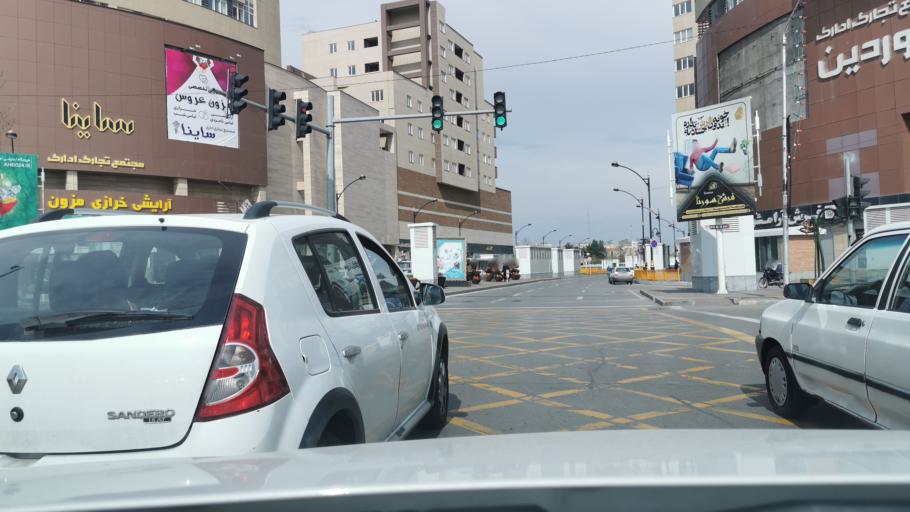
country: IR
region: Razavi Khorasan
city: Mashhad
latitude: 36.3123
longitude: 59.5902
